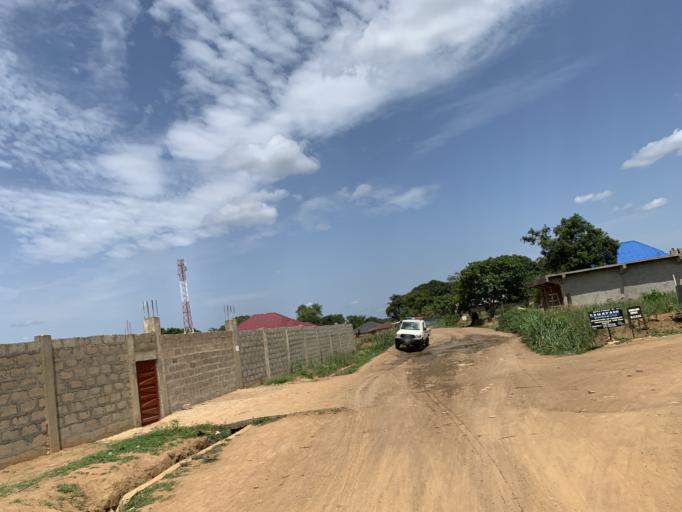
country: SL
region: Western Area
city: Waterloo
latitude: 8.3258
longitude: -13.0382
